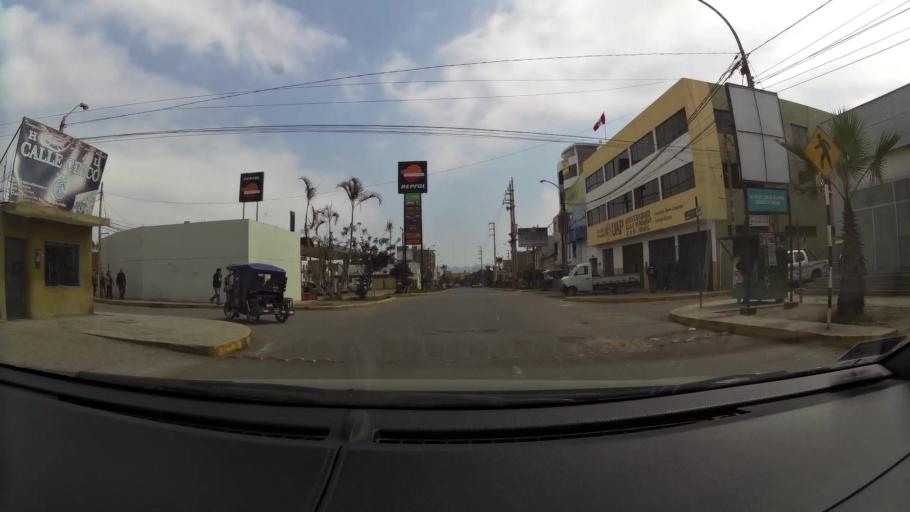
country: PE
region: Lima
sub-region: Provincia de Huaral
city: Huaral
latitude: -11.4979
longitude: -77.2142
